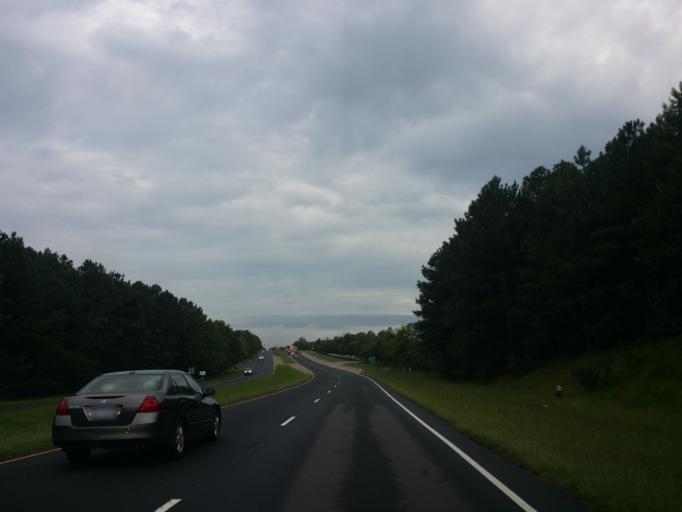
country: US
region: North Carolina
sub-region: Wake County
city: Morrisville
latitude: 35.9190
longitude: -78.8071
